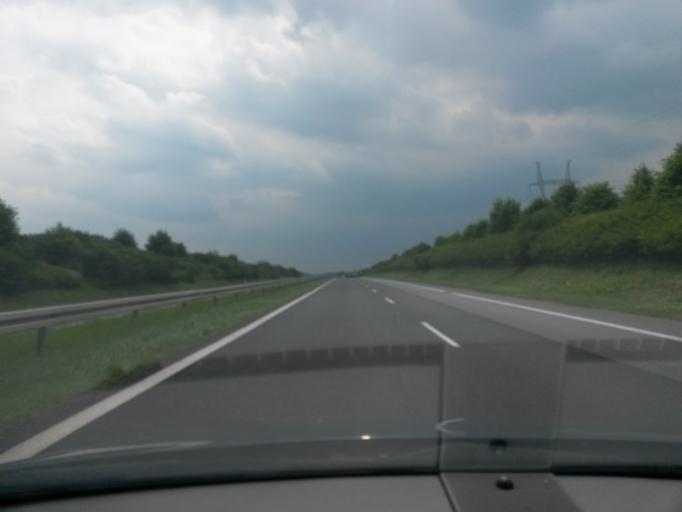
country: PL
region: Lodz Voivodeship
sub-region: Powiat radomszczanski
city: Radomsko
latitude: 51.0903
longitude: 19.3765
